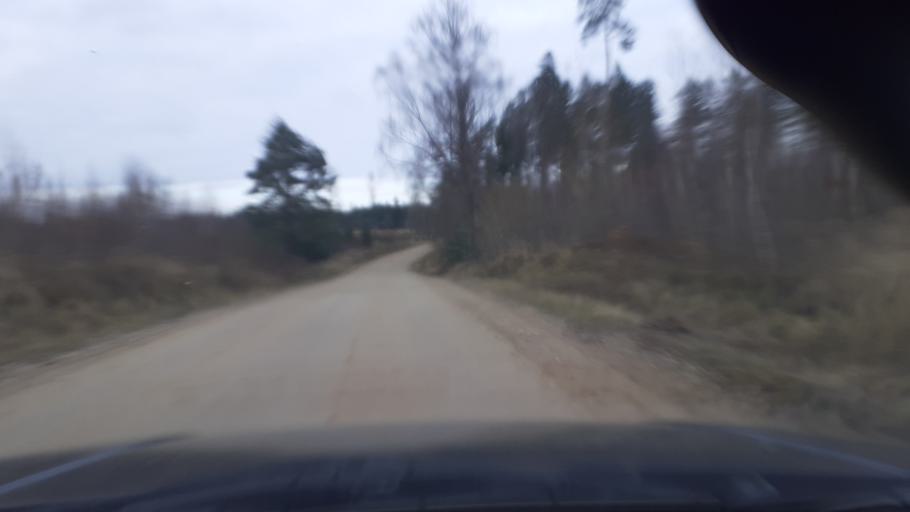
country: LV
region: Alsunga
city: Alsunga
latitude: 56.9622
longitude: 21.6528
